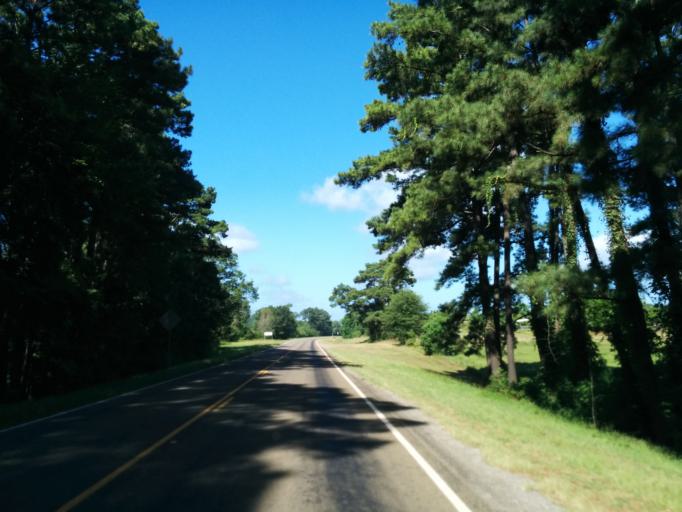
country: US
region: Texas
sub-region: Sabine County
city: Milam
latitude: 31.4174
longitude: -93.9812
